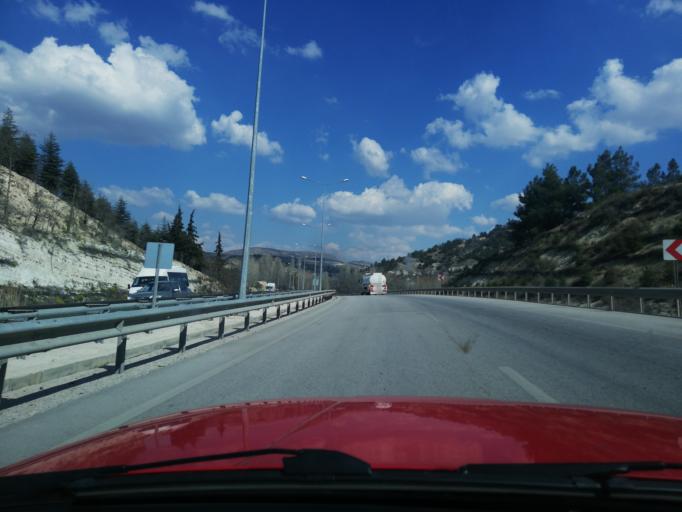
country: TR
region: Burdur
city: Burdur
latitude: 37.6978
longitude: 30.3299
